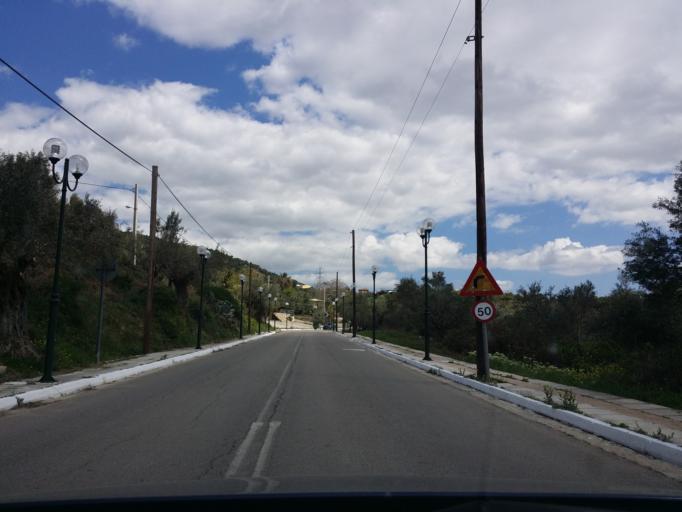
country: GR
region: Attica
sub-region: Nomarchia Dytikis Attikis
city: Fyli
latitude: 38.1102
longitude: 23.6658
